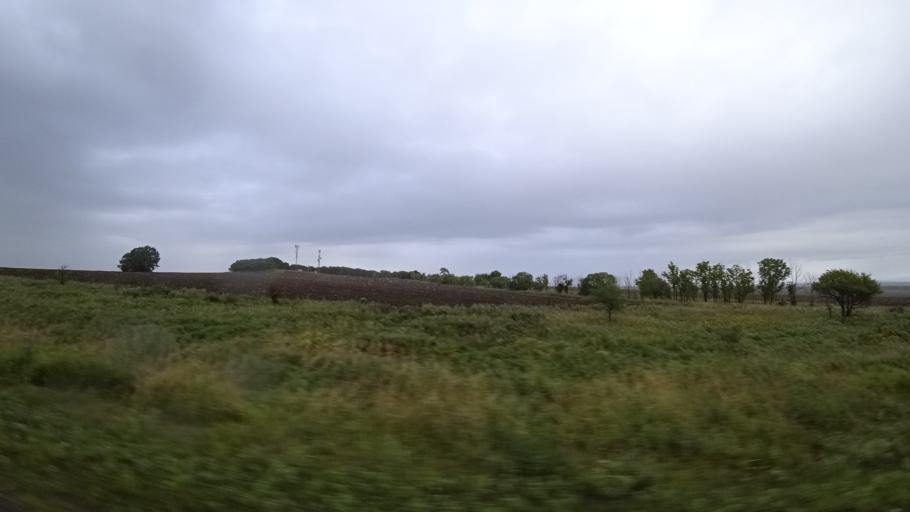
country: RU
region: Primorskiy
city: Chernigovka
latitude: 44.3659
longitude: 132.5370
